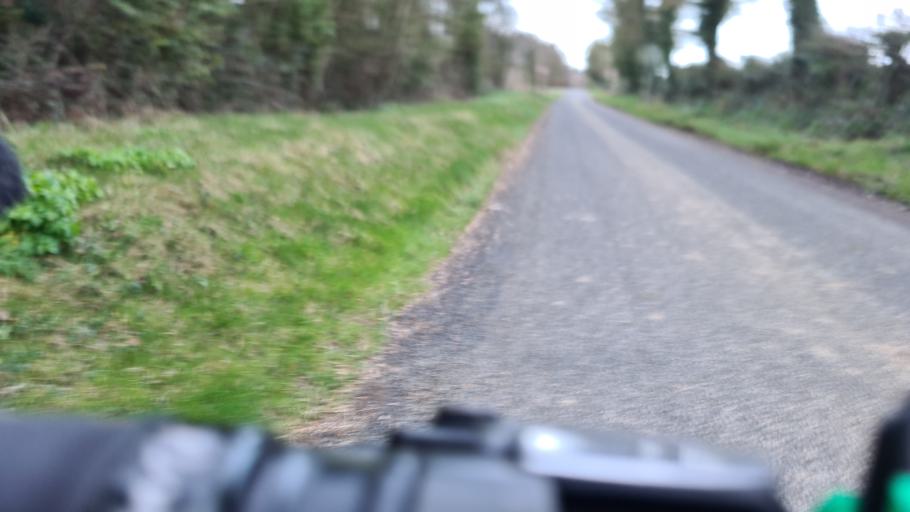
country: IE
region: Leinster
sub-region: Kildare
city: Maynooth
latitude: 53.3403
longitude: -6.6021
